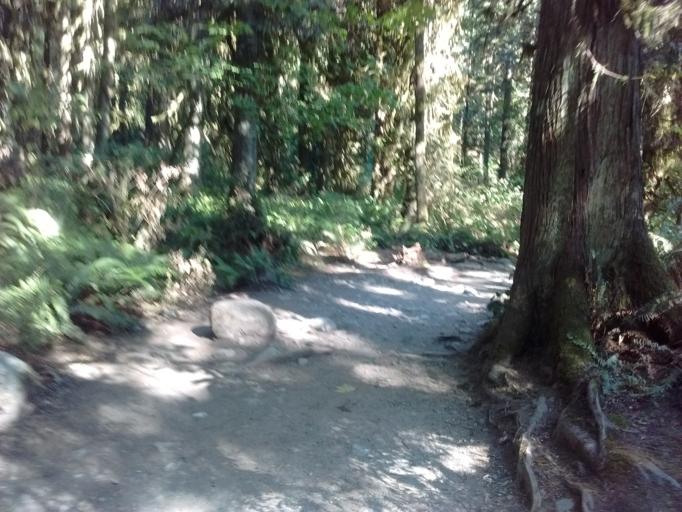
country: CA
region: British Columbia
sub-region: Fraser Valley Regional District
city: North Vancouver
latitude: 49.3468
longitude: -123.0197
